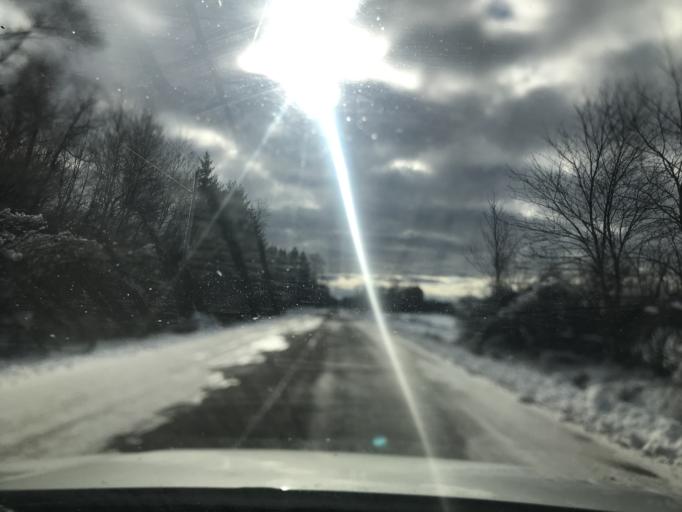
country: US
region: Wisconsin
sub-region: Marinette County
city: Peshtigo
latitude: 45.0946
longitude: -87.7227
